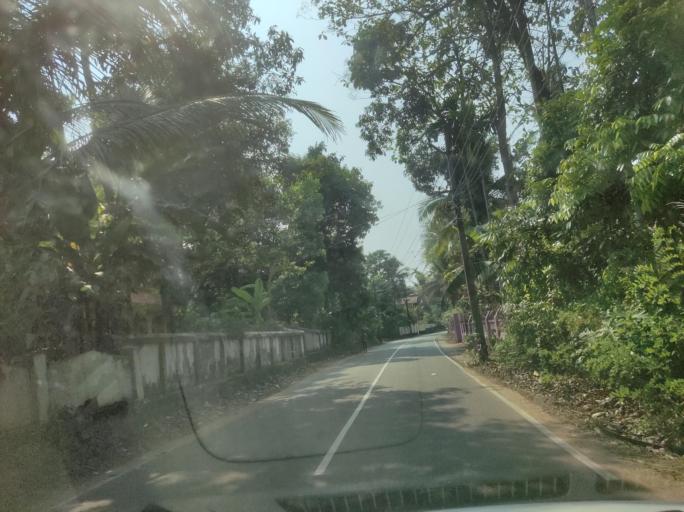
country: IN
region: Kerala
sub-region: Pattanamtitta
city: Tiruvalla
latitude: 9.3476
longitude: 76.5551
